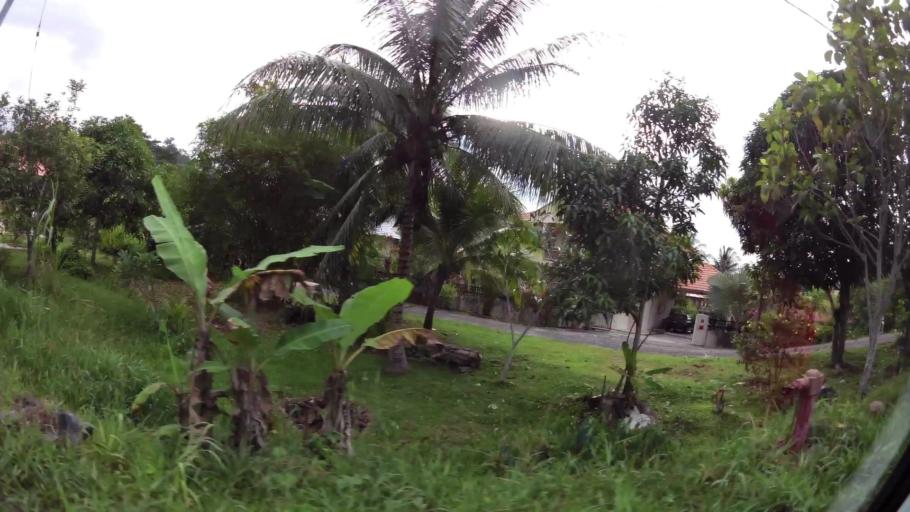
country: BN
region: Brunei and Muara
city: Bandar Seri Begawan
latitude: 4.9518
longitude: 114.9765
